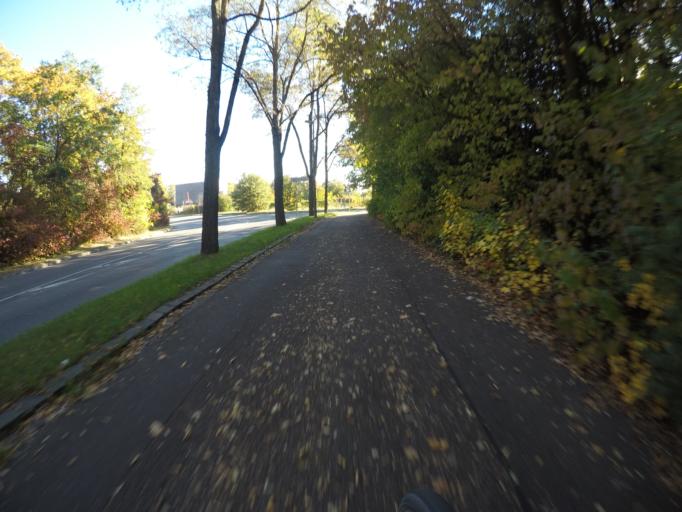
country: DE
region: Baden-Wuerttemberg
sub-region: Regierungsbezirk Stuttgart
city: Steinenbronn
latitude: 48.7214
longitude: 9.1091
